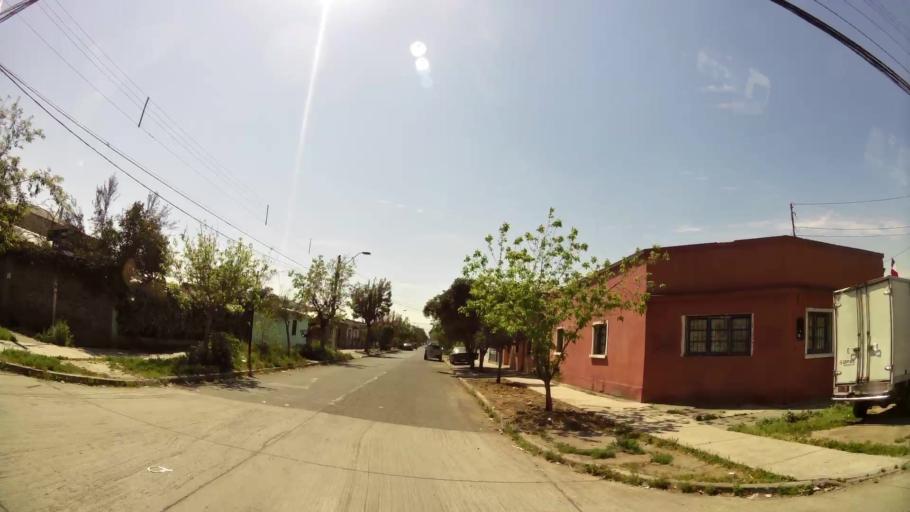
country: CL
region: Santiago Metropolitan
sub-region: Provincia de Santiago
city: La Pintana
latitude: -33.5338
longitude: -70.6468
